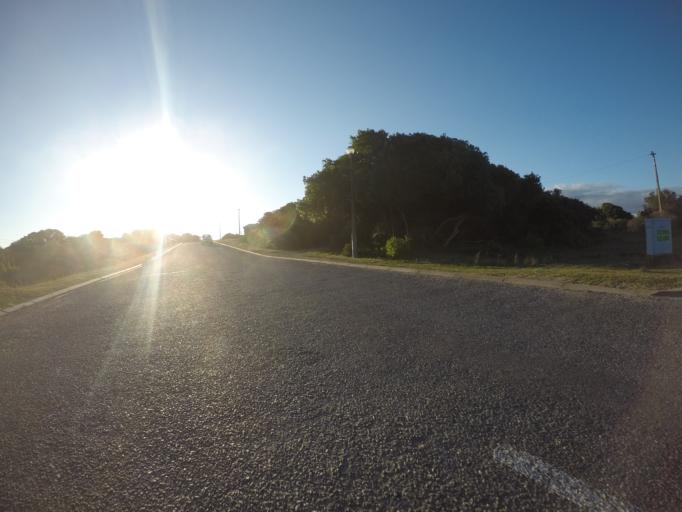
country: ZA
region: Western Cape
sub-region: Eden District Municipality
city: Riversdale
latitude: -34.3846
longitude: 21.4047
